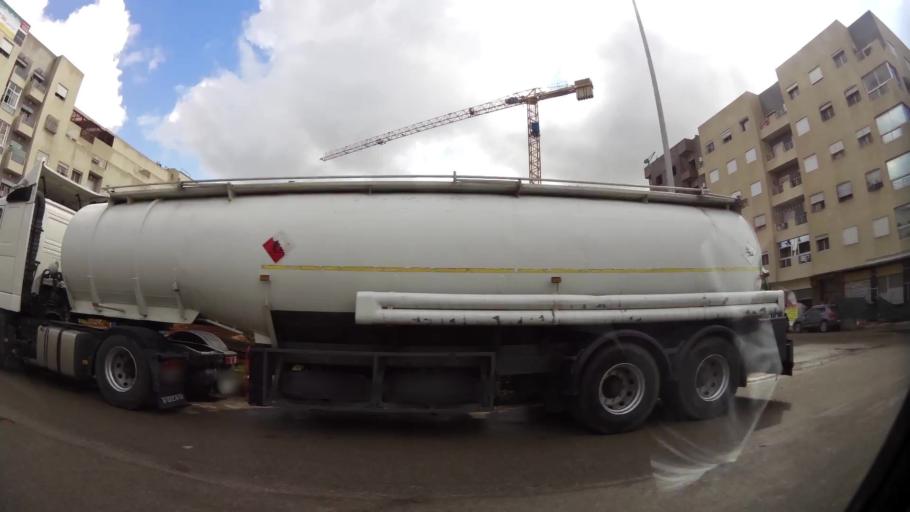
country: MA
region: Grand Casablanca
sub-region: Mediouna
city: Tit Mellil
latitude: 33.5458
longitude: -7.4822
